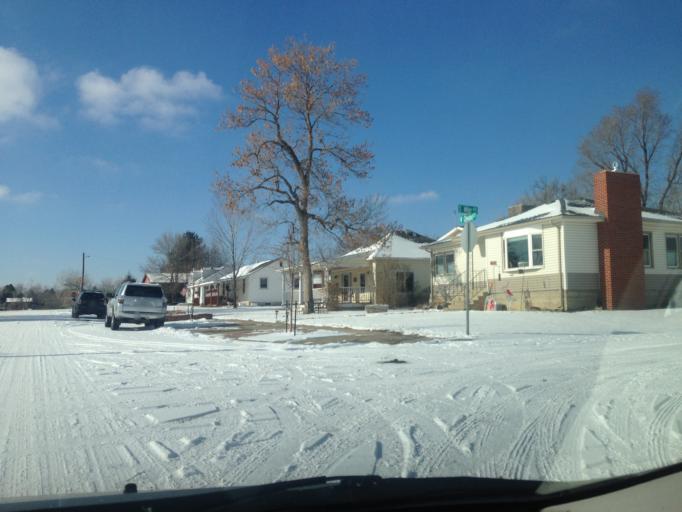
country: US
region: Colorado
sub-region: Boulder County
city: Lafayette
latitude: 39.9973
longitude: -105.0942
